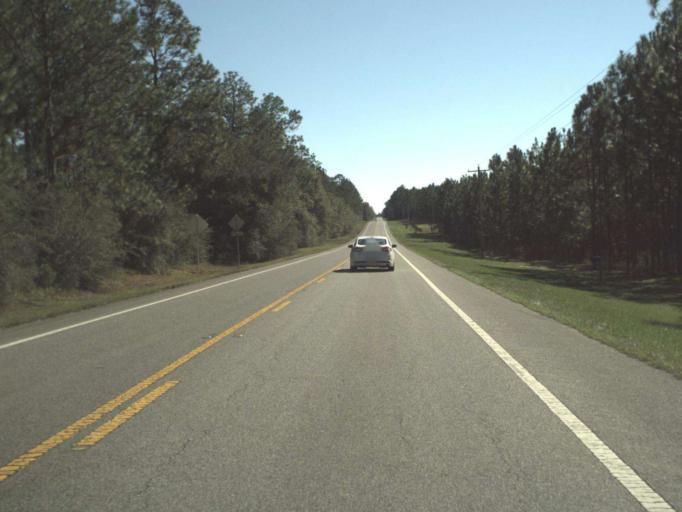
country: US
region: Florida
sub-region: Okaloosa County
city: Crestview
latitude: 30.8277
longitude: -86.7273
